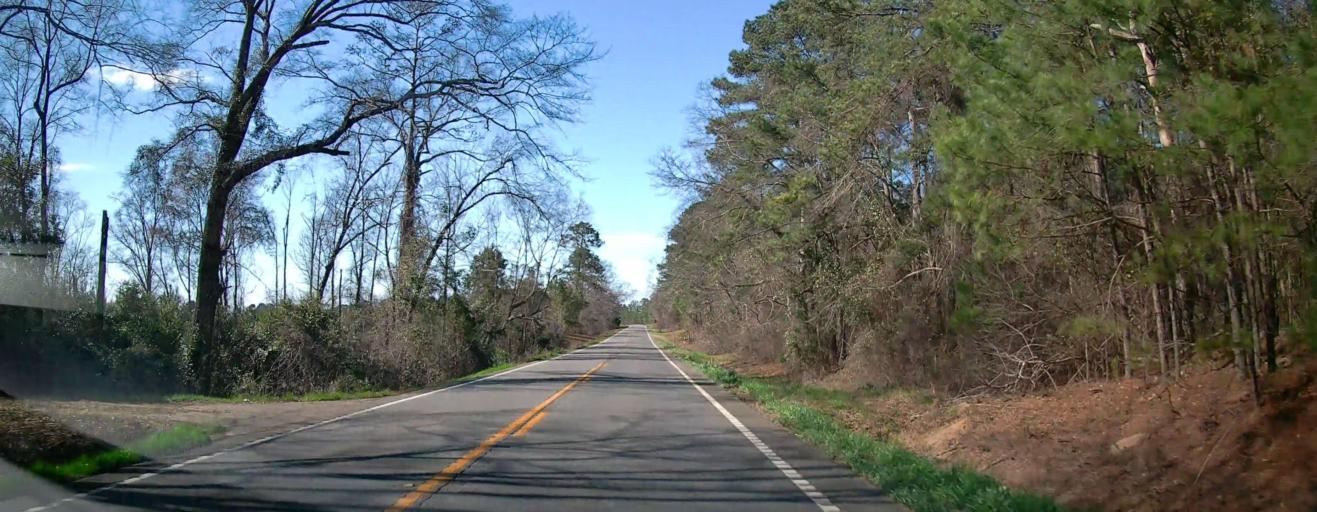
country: US
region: Georgia
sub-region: Macon County
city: Oglethorpe
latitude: 32.3403
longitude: -84.1311
